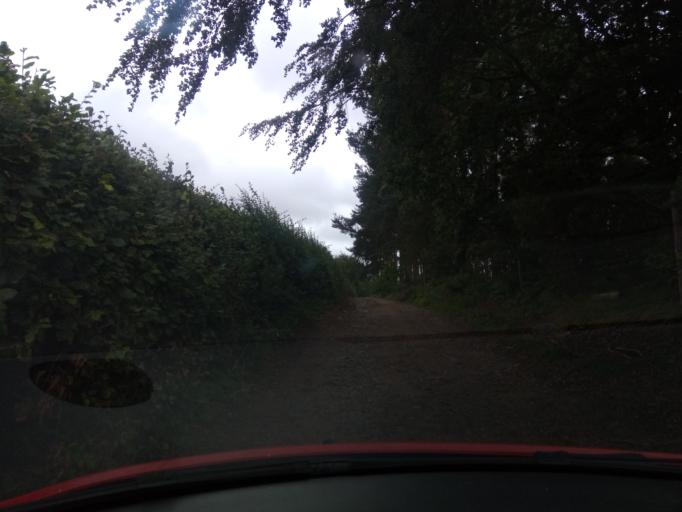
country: GB
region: Scotland
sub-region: The Scottish Borders
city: Jedburgh
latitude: 55.4870
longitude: -2.5185
